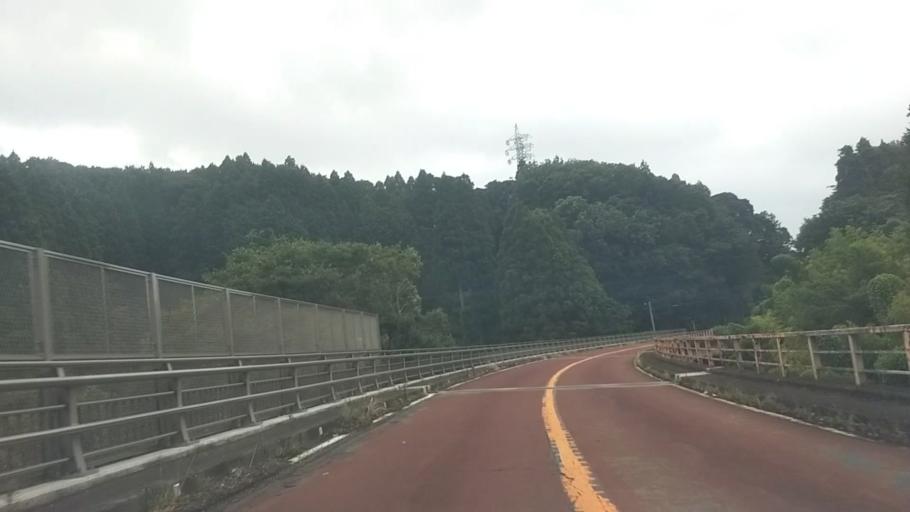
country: JP
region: Chiba
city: Kawaguchi
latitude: 35.2496
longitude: 140.0765
